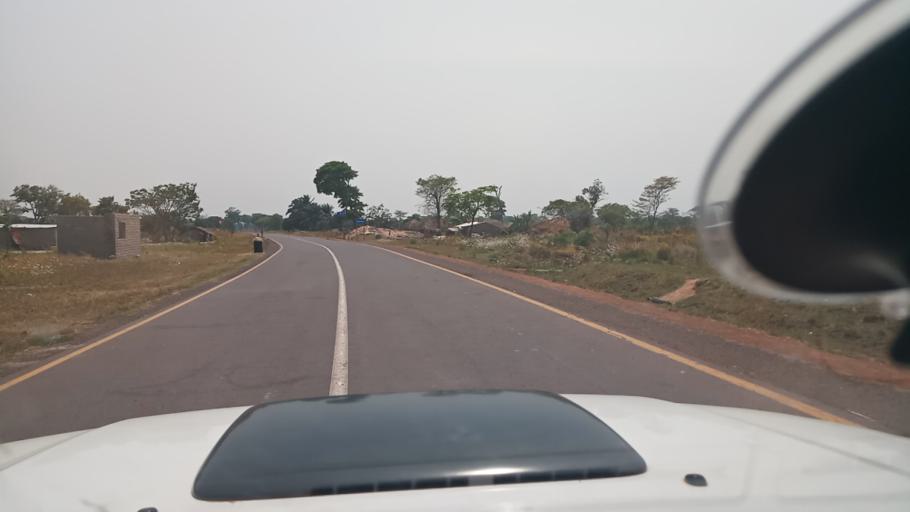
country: ZM
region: Luapula
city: Mwense
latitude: -10.7915
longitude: 28.2340
